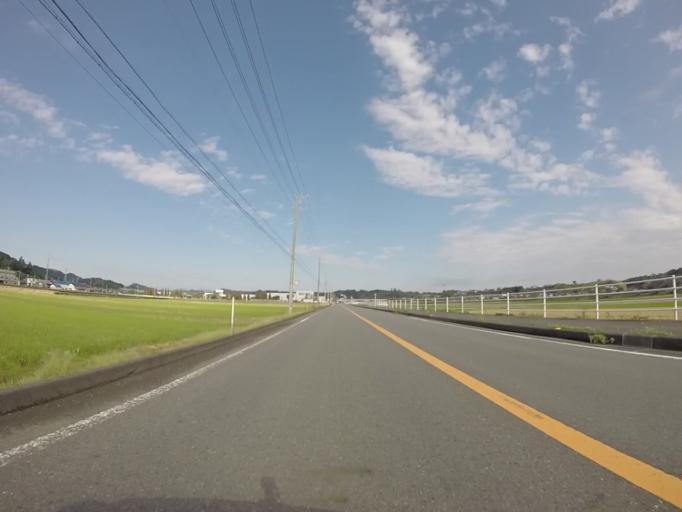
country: JP
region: Shizuoka
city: Shimada
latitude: 34.7683
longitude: 138.2334
